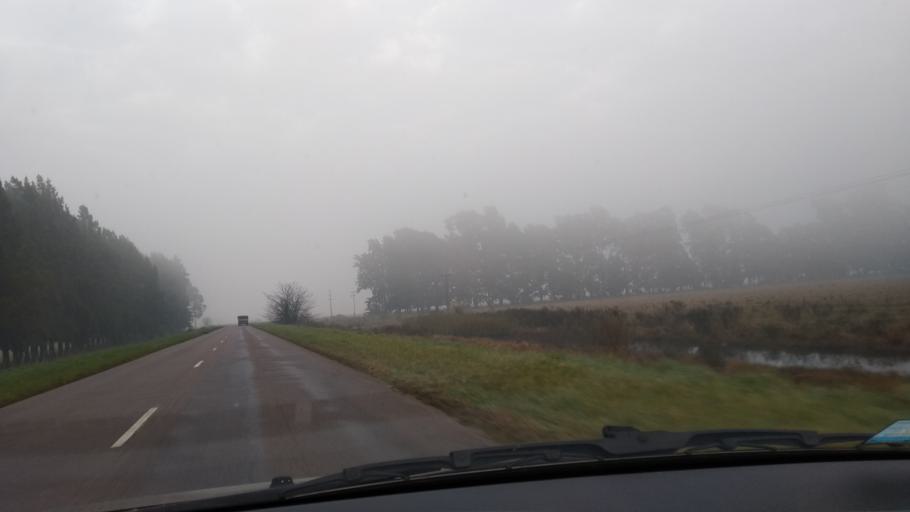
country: AR
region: Buenos Aires
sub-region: Partido de San Vicente
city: San Vicente
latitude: -35.2297
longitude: -58.4533
